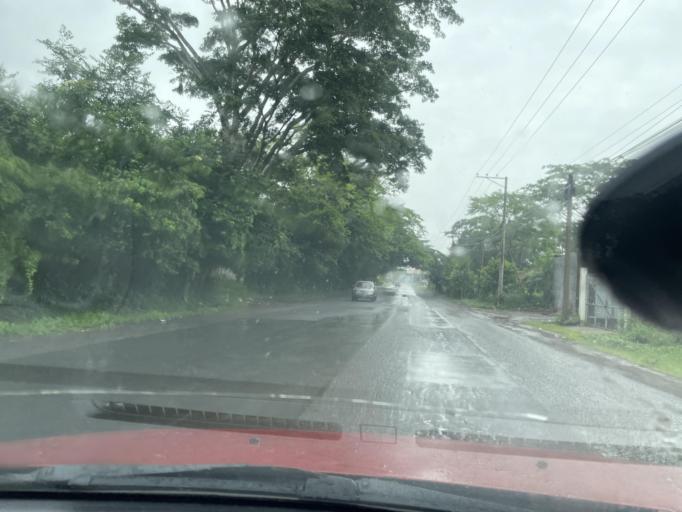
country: SV
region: La Union
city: Santa Rosa de Lima
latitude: 13.6097
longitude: -87.9060
